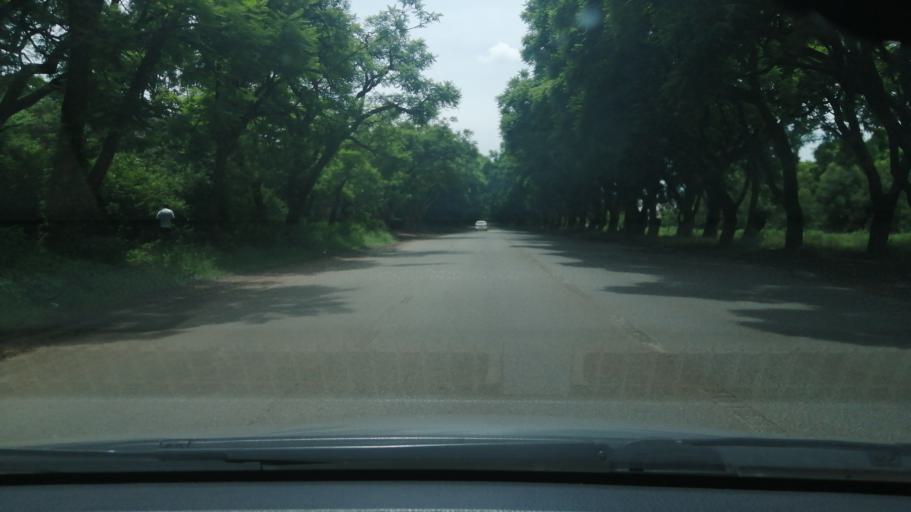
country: ZW
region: Harare
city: Harare
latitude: -17.8088
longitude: 31.0404
